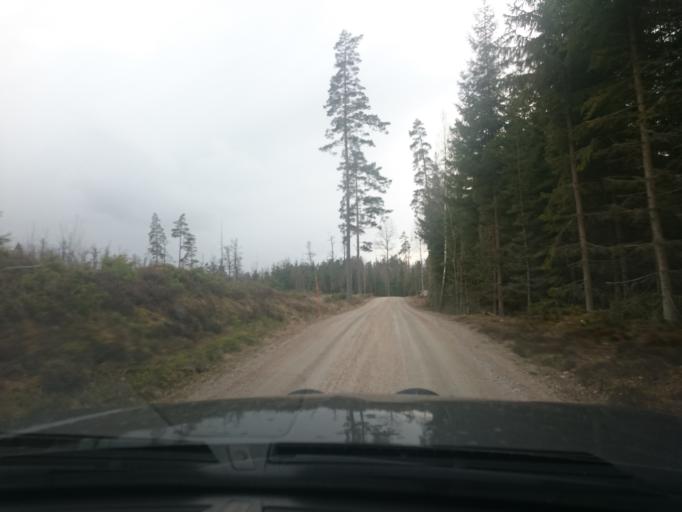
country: SE
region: Joenkoeping
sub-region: Vetlanda Kommun
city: Vetlanda
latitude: 57.2957
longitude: 15.1356
